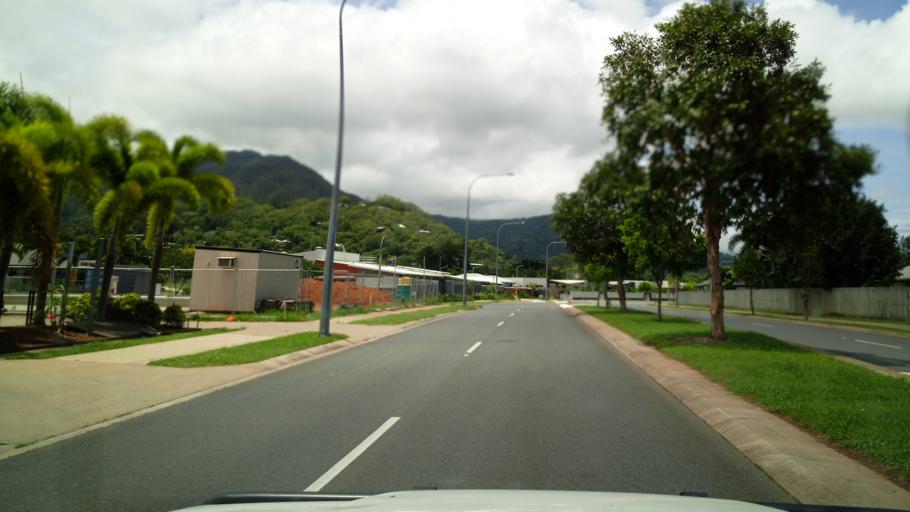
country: AU
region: Queensland
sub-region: Cairns
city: Yorkeys Knob
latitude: -16.8334
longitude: 145.6956
